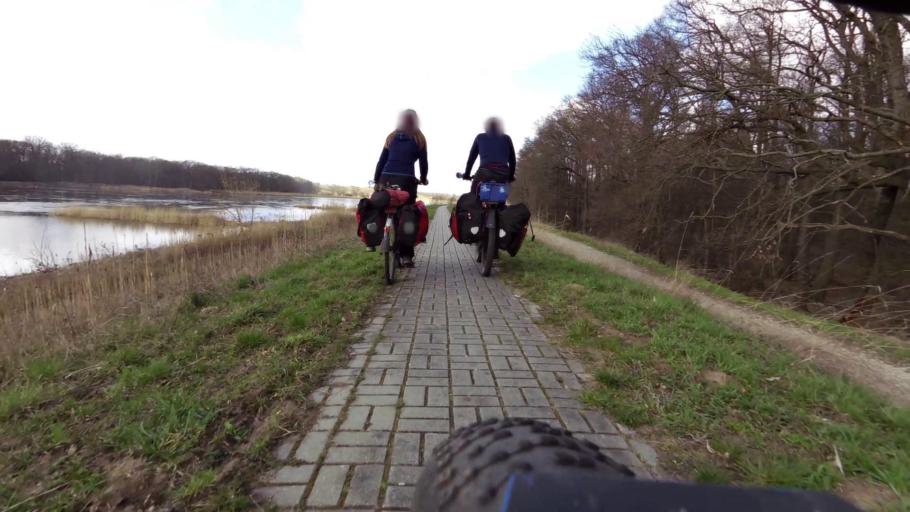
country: PL
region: Lubusz
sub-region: Powiat slubicki
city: Slubice
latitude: 52.3870
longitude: 14.5436
